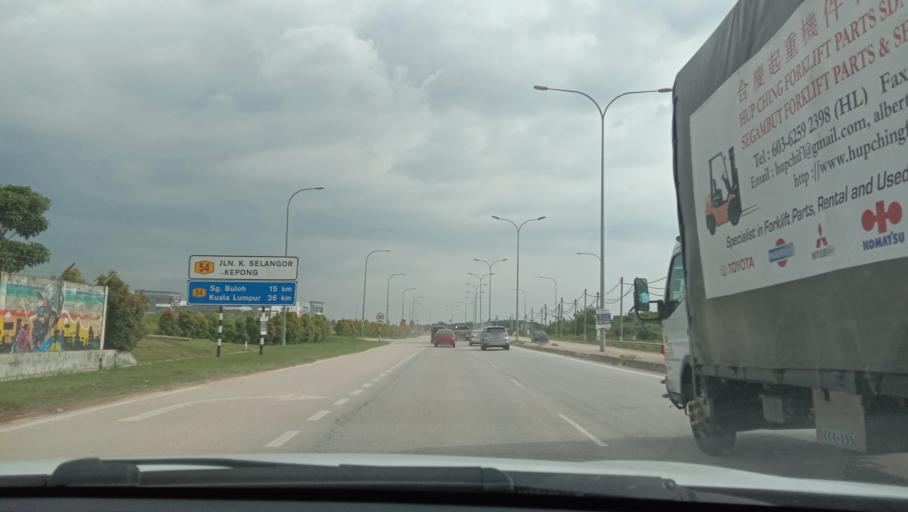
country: MY
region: Selangor
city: Ladang Seri Kundang
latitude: 3.2455
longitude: 101.4730
